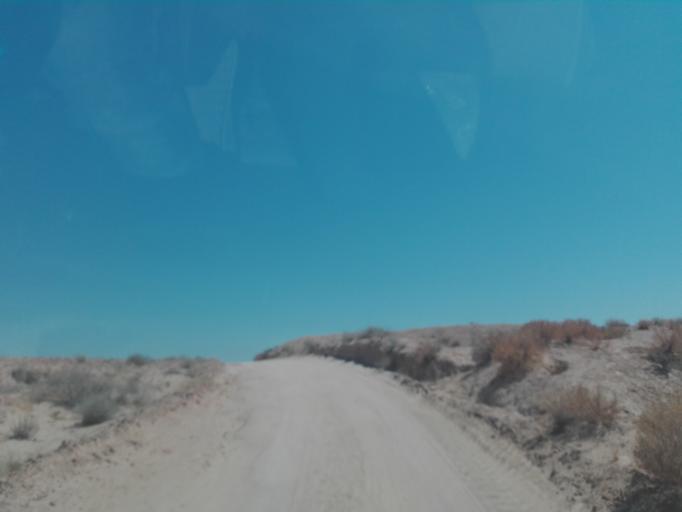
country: TN
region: Safaqis
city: Skhira
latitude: 34.3776
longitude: 9.9111
